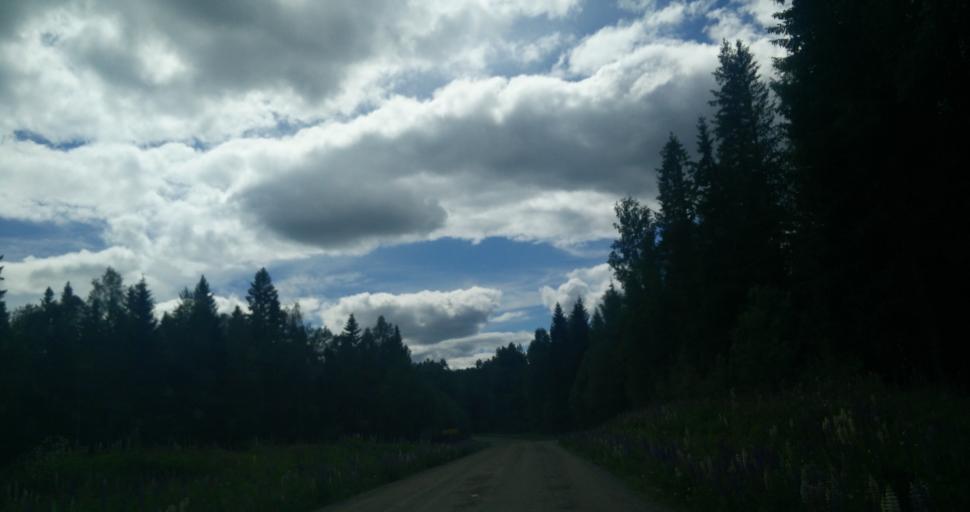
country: SE
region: Gaevleborg
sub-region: Nordanstigs Kommun
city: Bergsjoe
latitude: 62.1180
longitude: 17.0998
